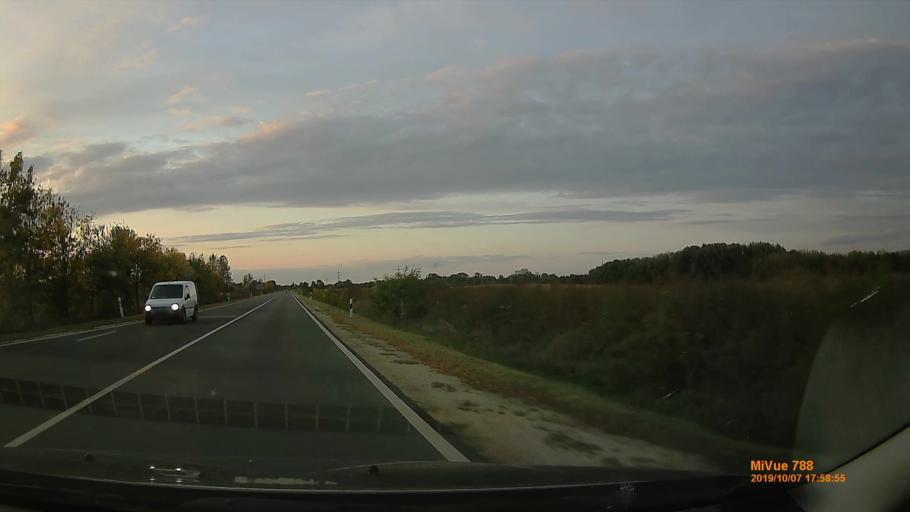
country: HU
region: Bacs-Kiskun
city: Kecskemet
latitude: 46.8723
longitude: 19.6847
